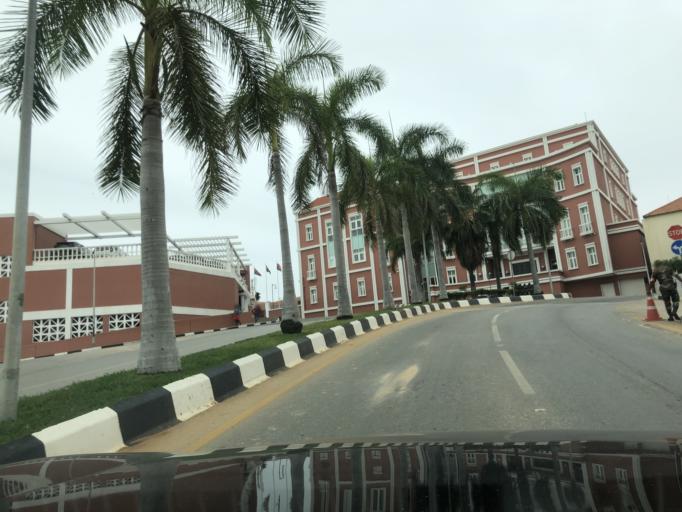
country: AO
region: Luanda
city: Luanda
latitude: -8.8194
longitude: 13.2248
